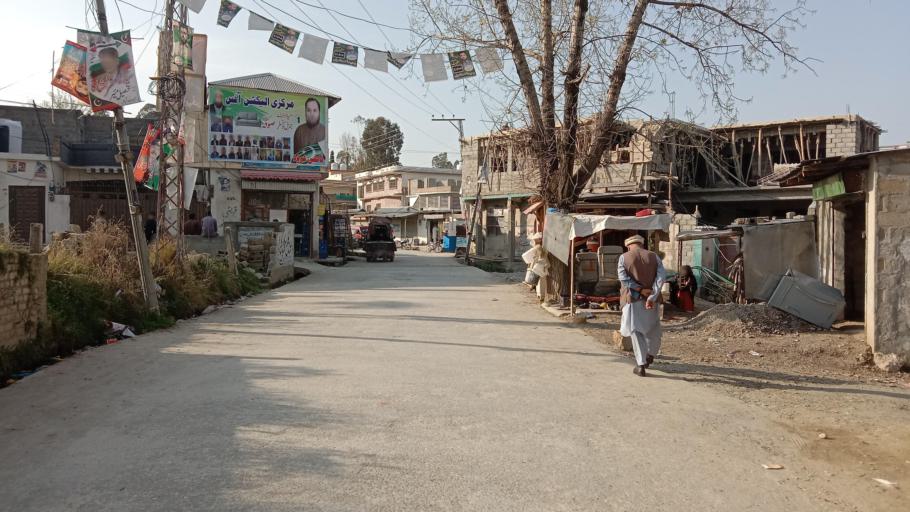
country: PK
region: Khyber Pakhtunkhwa
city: Abbottabad
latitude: 34.2022
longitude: 73.2252
